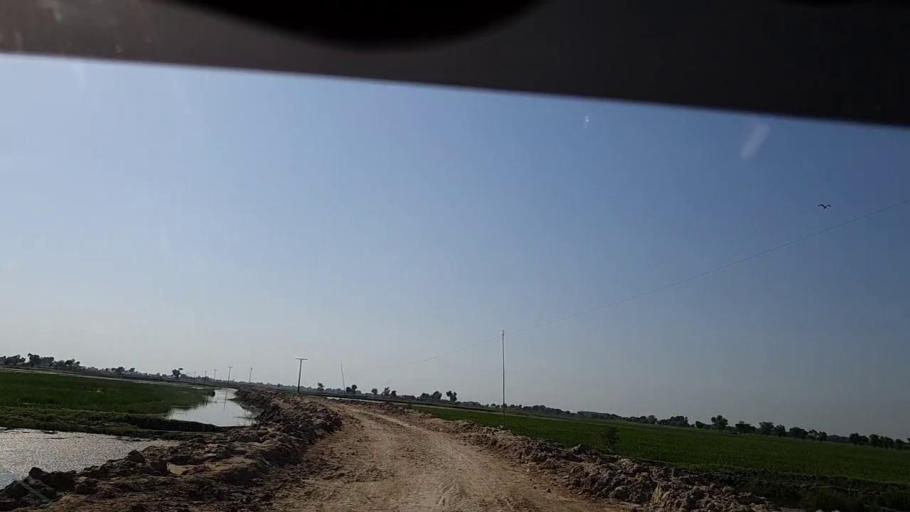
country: PK
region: Sindh
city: Tangwani
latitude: 28.3615
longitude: 69.0224
